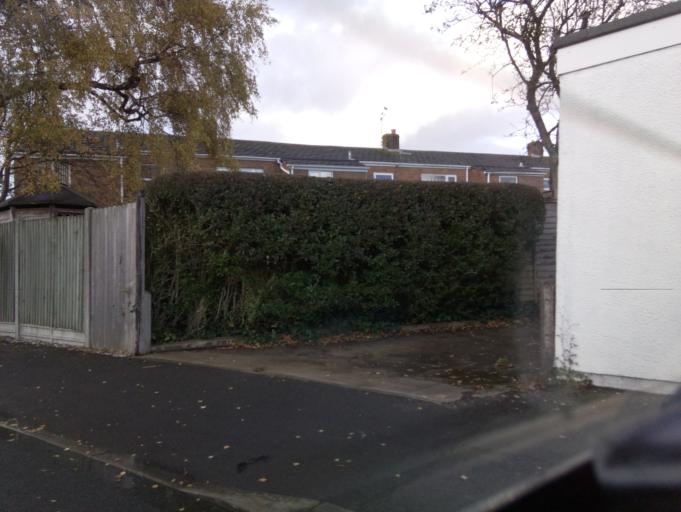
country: GB
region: England
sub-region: South Gloucestershire
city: Almondsbury
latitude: 51.5756
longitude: -2.5644
